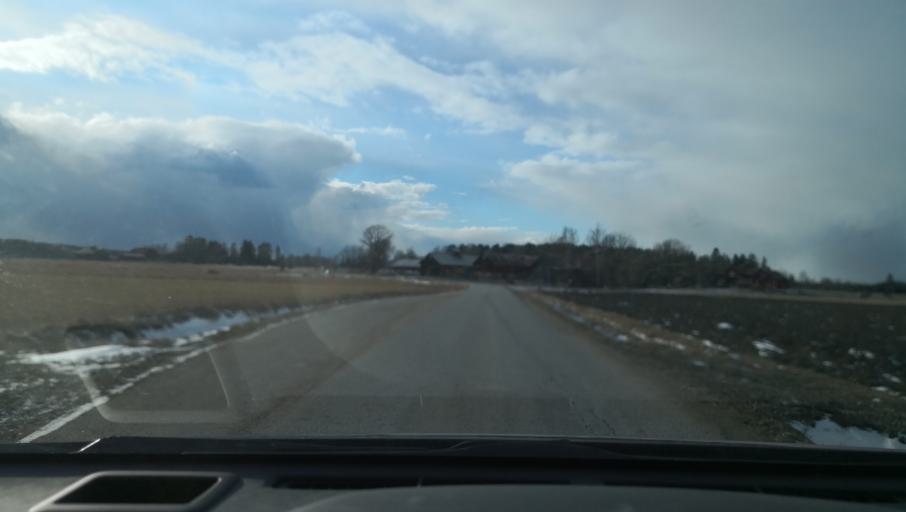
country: SE
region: Uppsala
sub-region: Enkopings Kommun
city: Irsta
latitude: 59.6960
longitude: 16.9682
